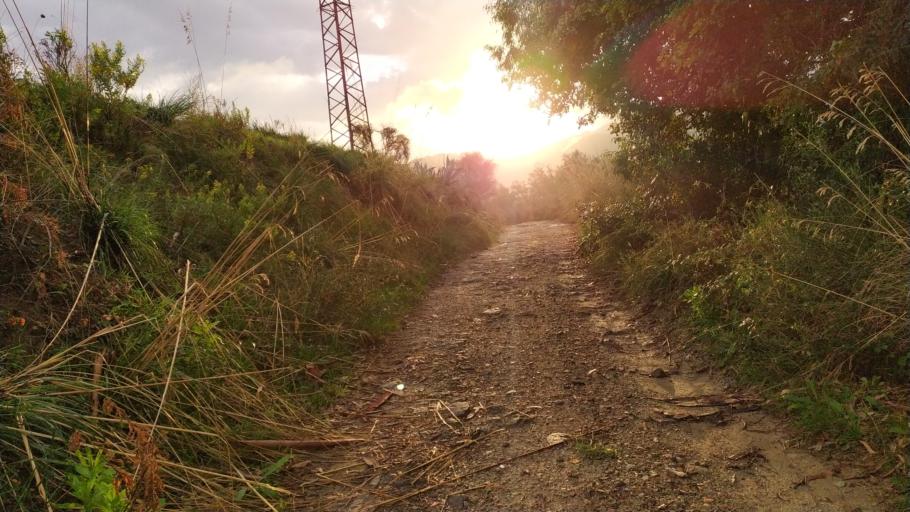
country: IT
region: Sicily
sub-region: Messina
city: Villafranca Tirrena
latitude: 38.2168
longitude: 15.4715
